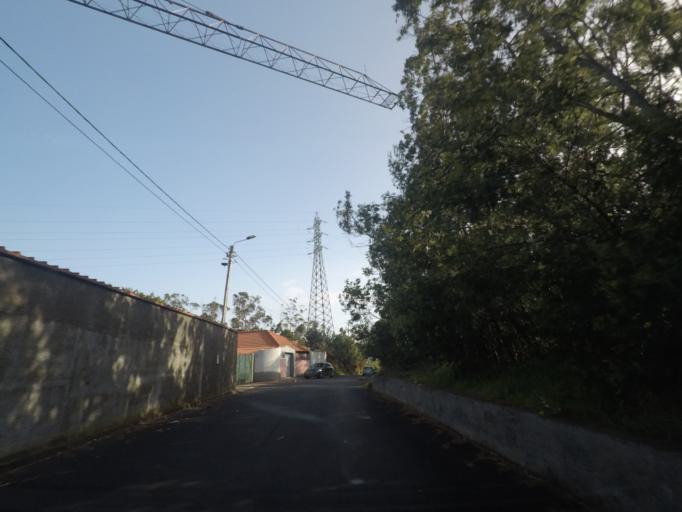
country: PT
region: Madeira
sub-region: Ribeira Brava
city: Campanario
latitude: 32.6679
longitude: -17.0025
